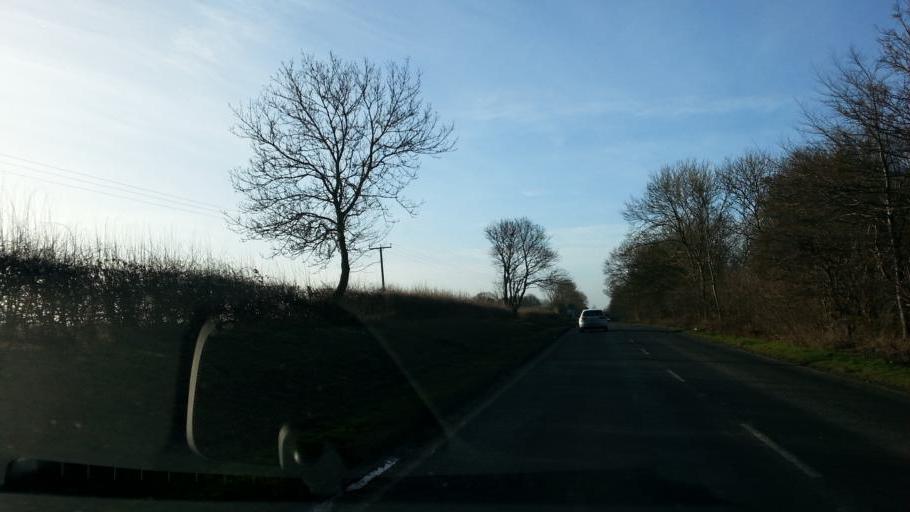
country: GB
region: England
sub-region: Lincolnshire
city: Grantham
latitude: 52.9060
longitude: -0.5856
